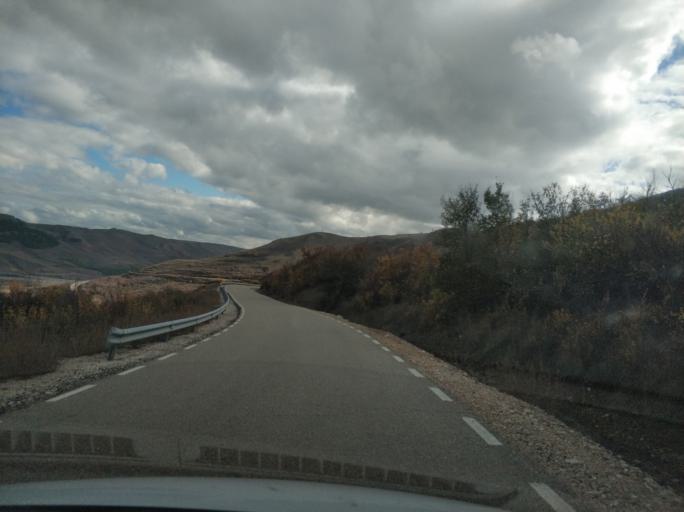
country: ES
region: Castille and Leon
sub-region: Provincia de Soria
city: Medinaceli
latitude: 41.1661
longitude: -2.4350
